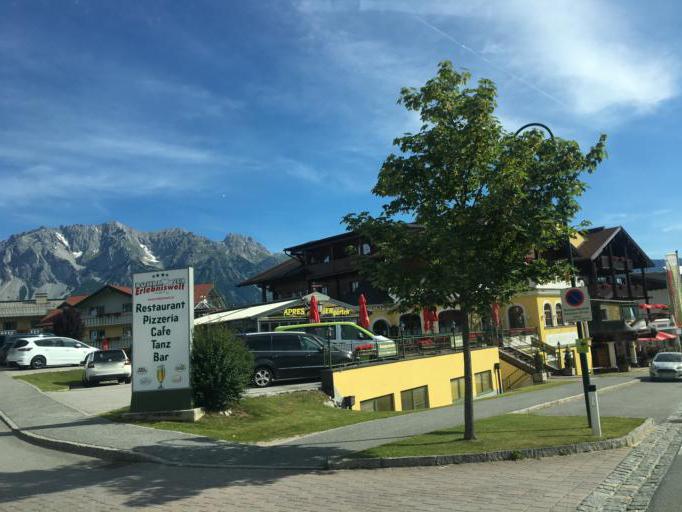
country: AT
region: Styria
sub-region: Politischer Bezirk Liezen
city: Schladming
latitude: 47.3828
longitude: 13.6685
